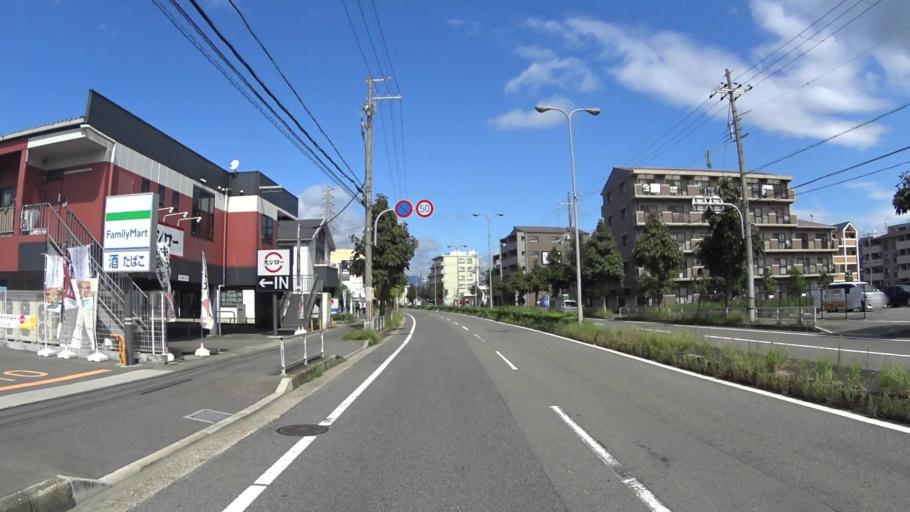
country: JP
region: Kyoto
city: Muko
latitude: 34.9769
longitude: 135.7128
